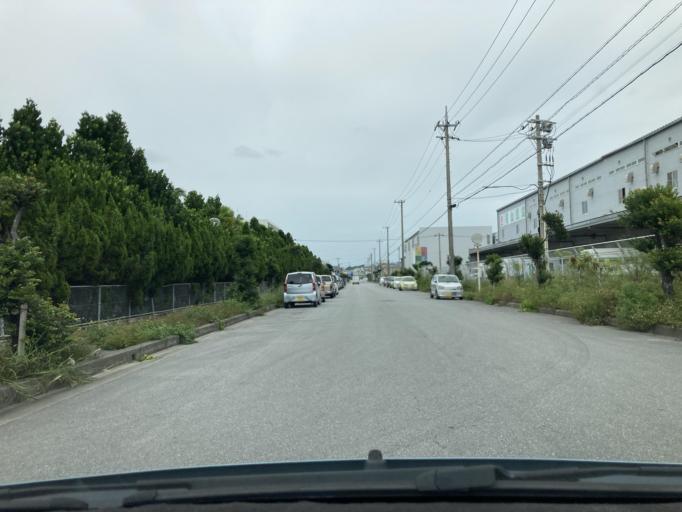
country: JP
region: Okinawa
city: Itoman
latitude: 26.1375
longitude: 127.6529
